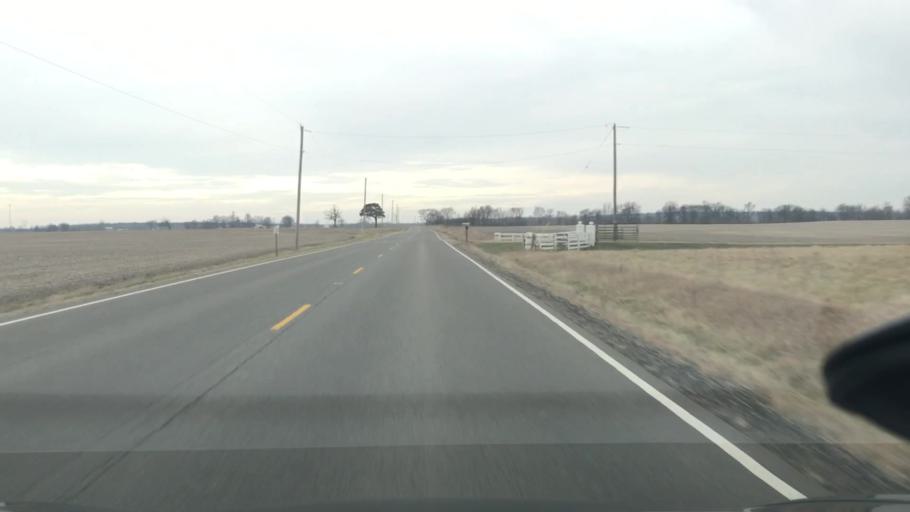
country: US
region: Ohio
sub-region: Madison County
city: Bethel
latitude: 39.7972
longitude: -83.3257
